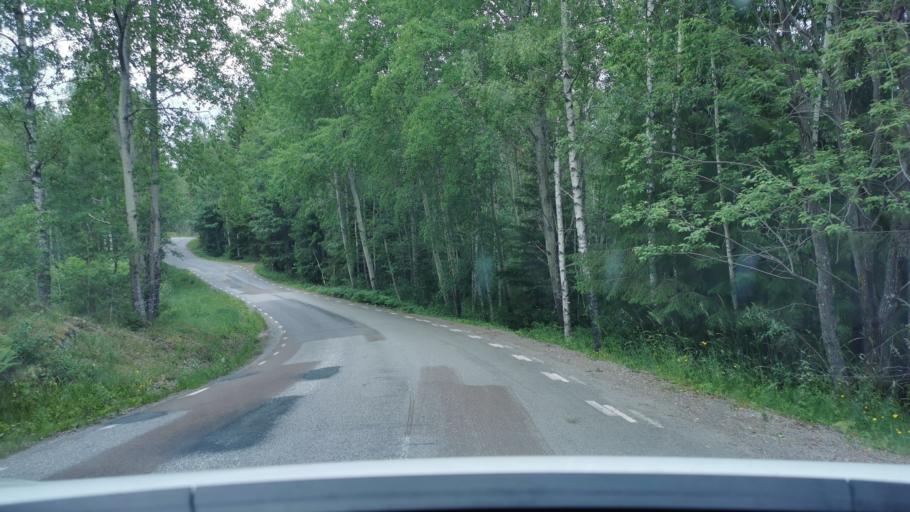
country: SE
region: Vaestra Goetaland
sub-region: Bengtsfors Kommun
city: Dals Langed
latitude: 58.8571
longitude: 12.4034
